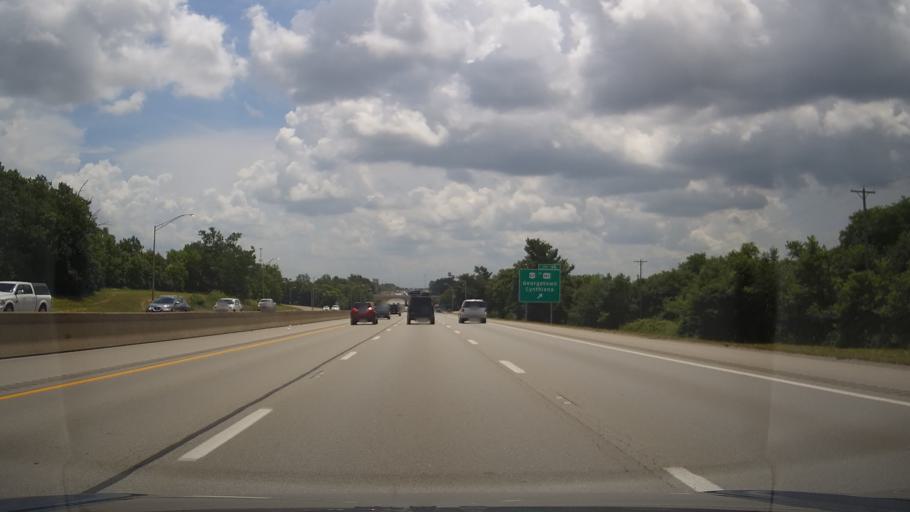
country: US
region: Kentucky
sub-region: Scott County
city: Georgetown
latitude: 38.2309
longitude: -84.5409
